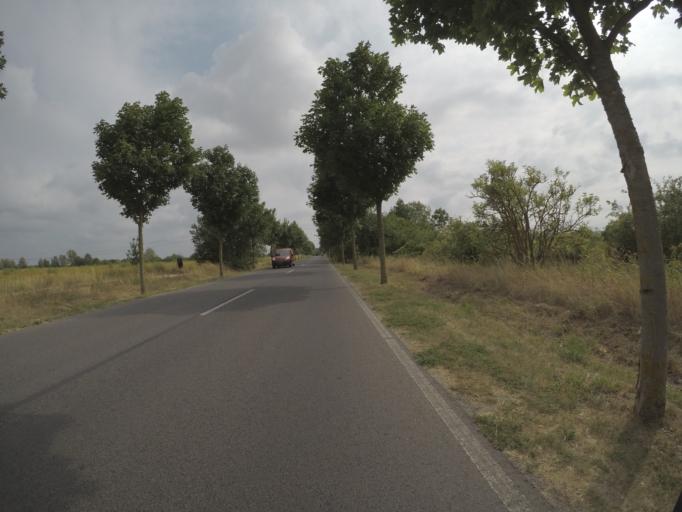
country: DE
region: Brandenburg
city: Schonefeld
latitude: 52.3984
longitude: 13.5009
